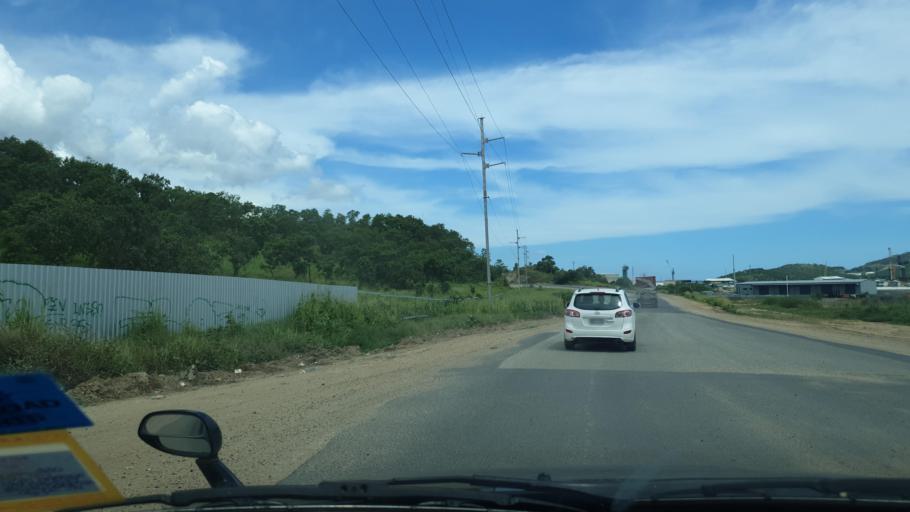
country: PG
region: National Capital
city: Port Moresby
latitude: -9.4155
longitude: 147.1019
